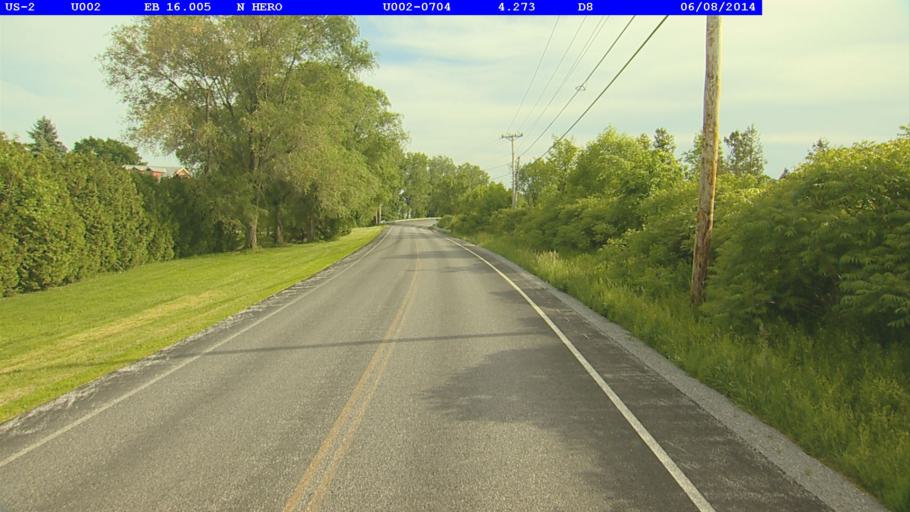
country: US
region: Vermont
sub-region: Grand Isle County
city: North Hero
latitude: 44.8314
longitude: -73.2740
